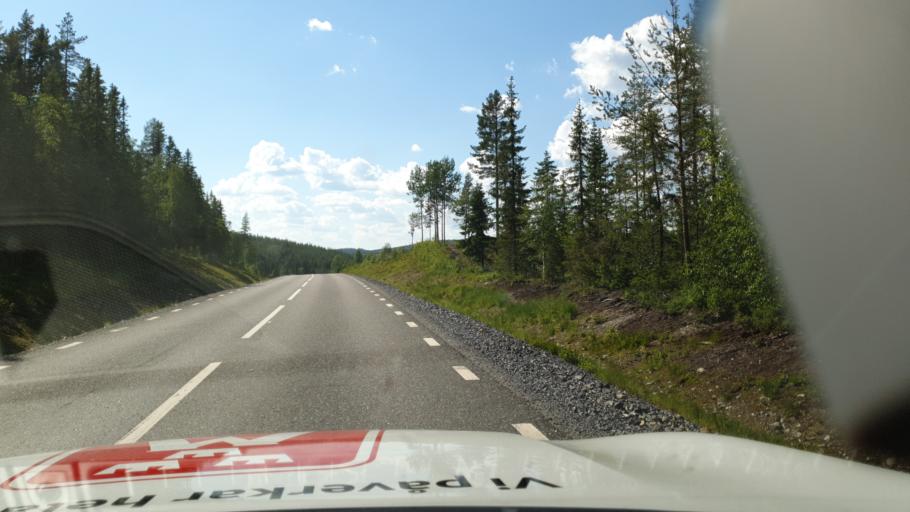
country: SE
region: Vaesterbotten
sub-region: Vindelns Kommun
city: Vindeln
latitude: 64.2522
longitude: 19.9776
